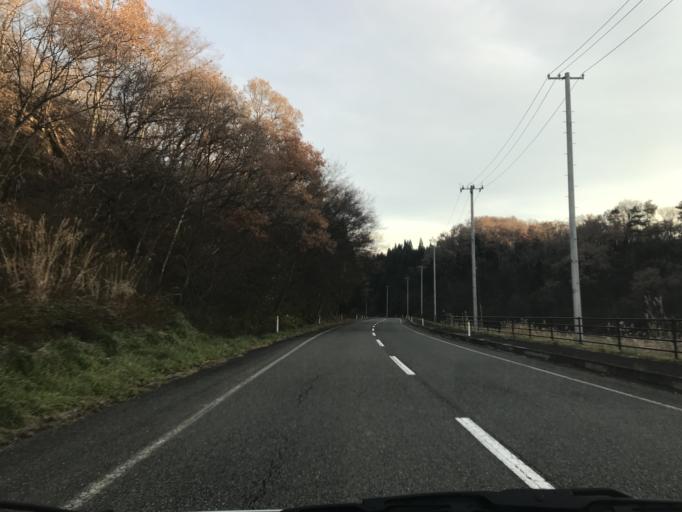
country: JP
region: Iwate
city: Ichinoseki
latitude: 38.9757
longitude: 141.0725
